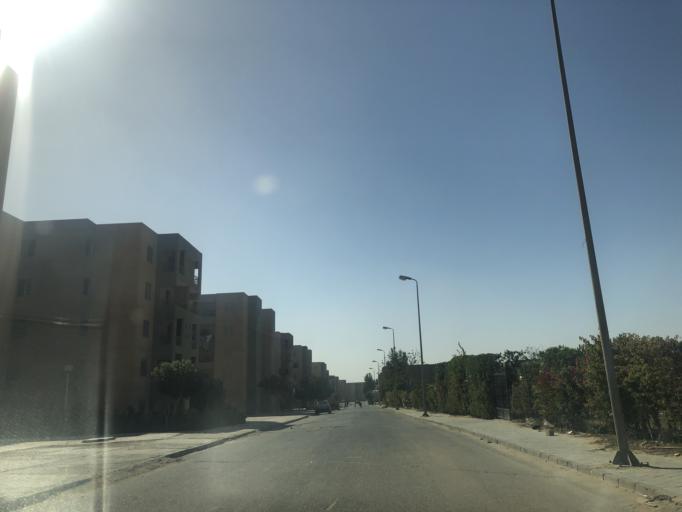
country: EG
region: Al Jizah
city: Madinat Sittah Uktubar
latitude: 29.9231
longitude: 30.9378
